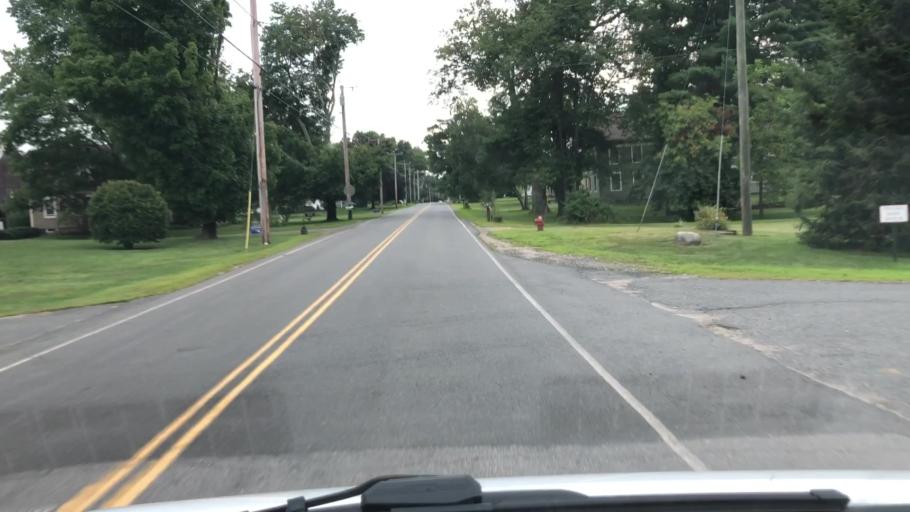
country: US
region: Massachusetts
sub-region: Franklin County
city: Whately
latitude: 42.4456
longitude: -72.6152
